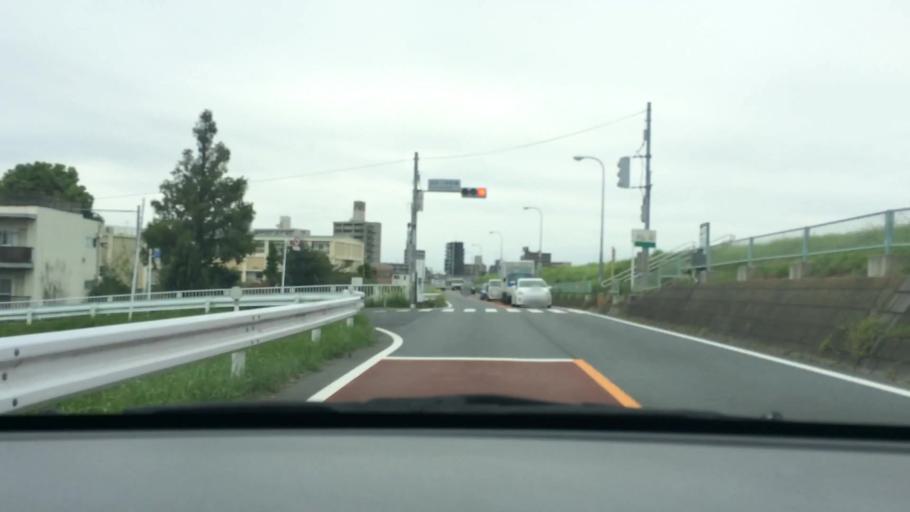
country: JP
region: Chiba
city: Matsudo
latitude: 35.7645
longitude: 139.8790
